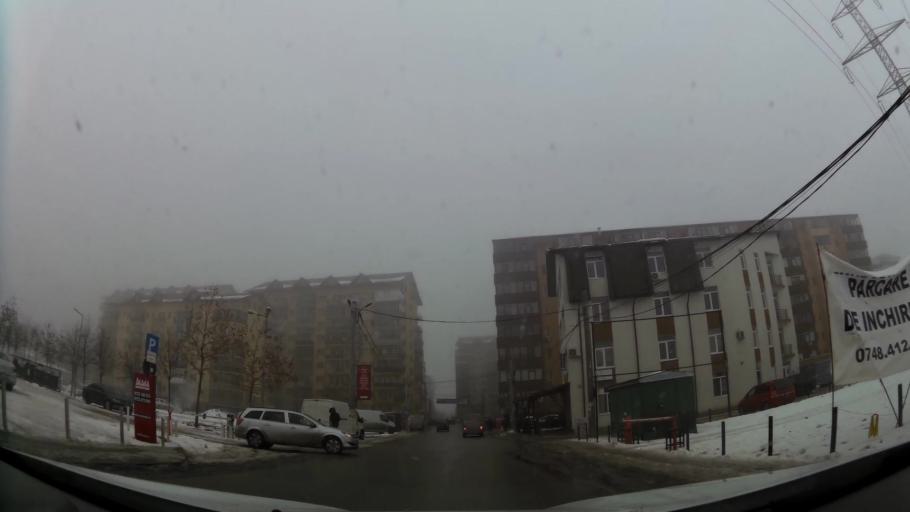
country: RO
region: Ilfov
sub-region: Comuna Chiajna
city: Chiajna
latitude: 44.4443
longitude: 25.9832
